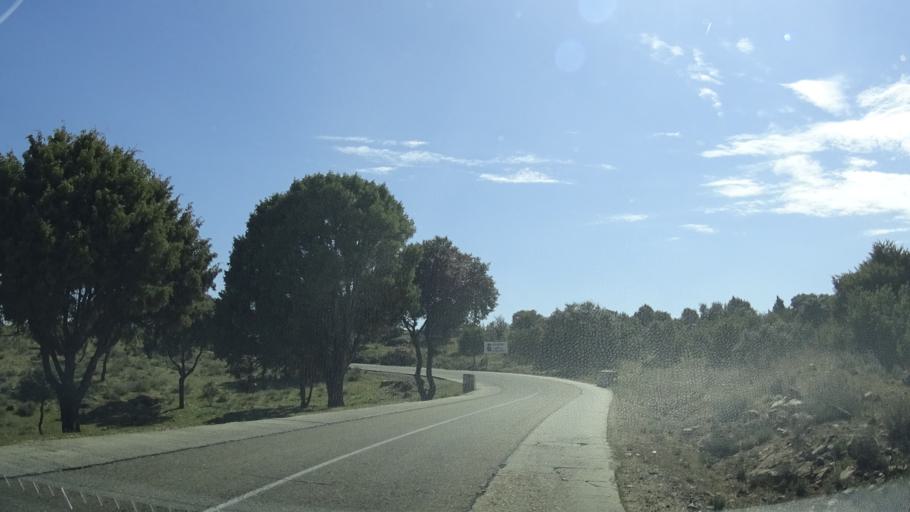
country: ES
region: Madrid
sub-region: Provincia de Madrid
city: Hoyo de Manzanares
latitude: 40.6348
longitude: -3.8571
